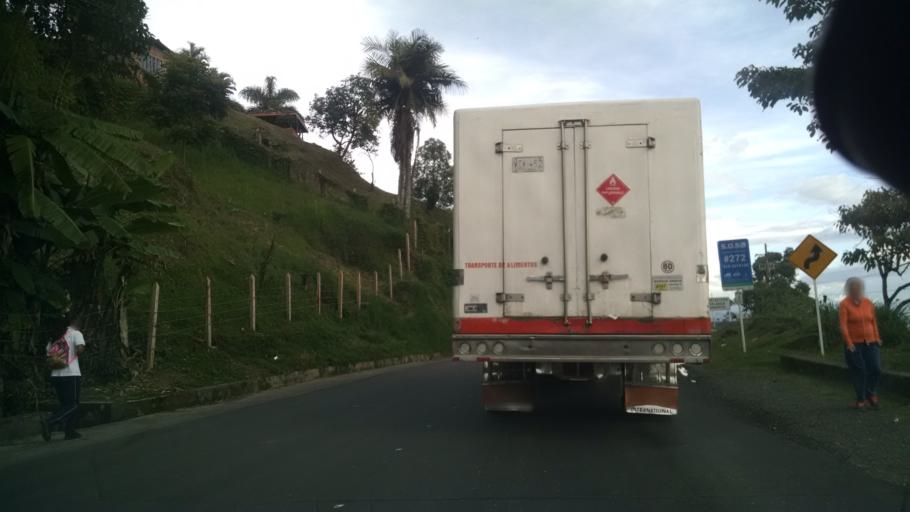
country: CO
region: Antioquia
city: Santa Barbara
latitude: 5.9165
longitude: -75.5787
